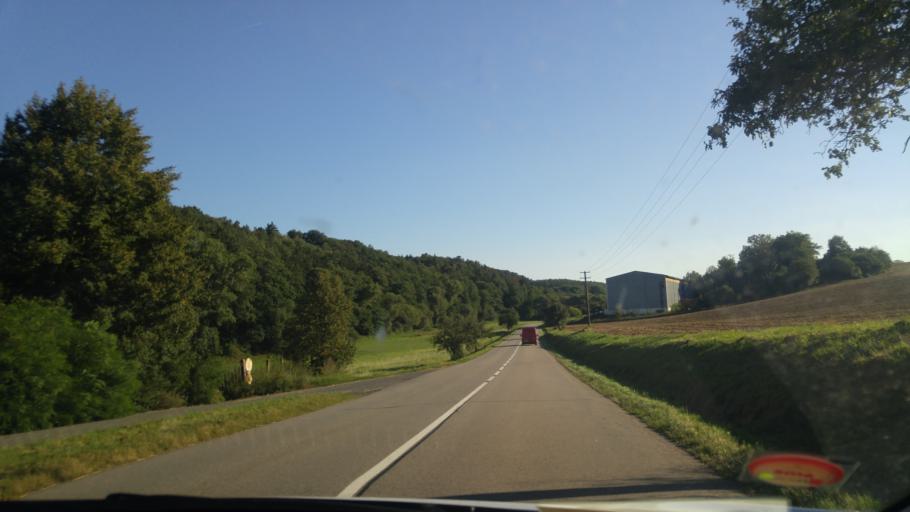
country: CZ
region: South Moravian
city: Veverska Bityska
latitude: 49.2491
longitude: 16.4479
